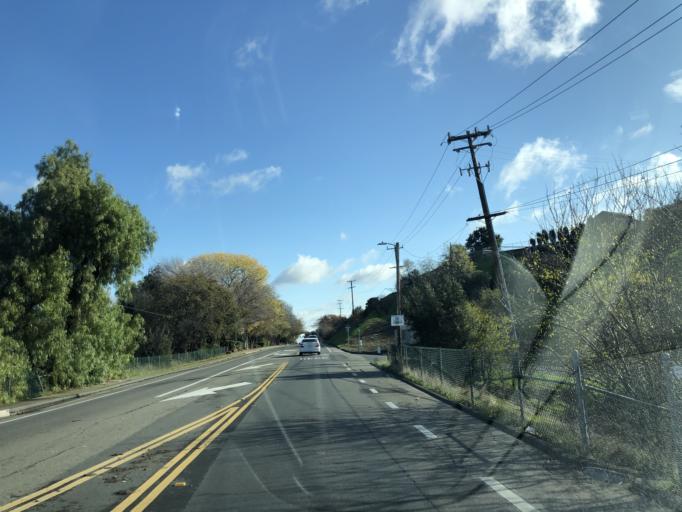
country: US
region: California
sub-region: Contra Costa County
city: Pittsburg
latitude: 37.9980
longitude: -121.8920
